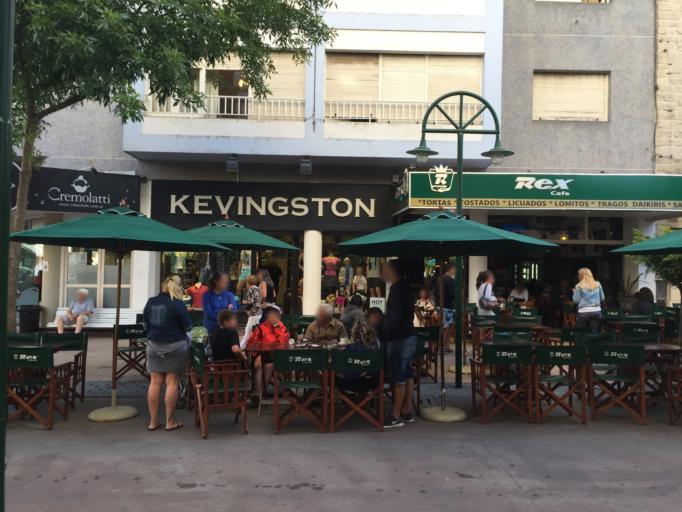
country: AR
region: Buenos Aires
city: Miramar
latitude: -38.2722
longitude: -57.8355
